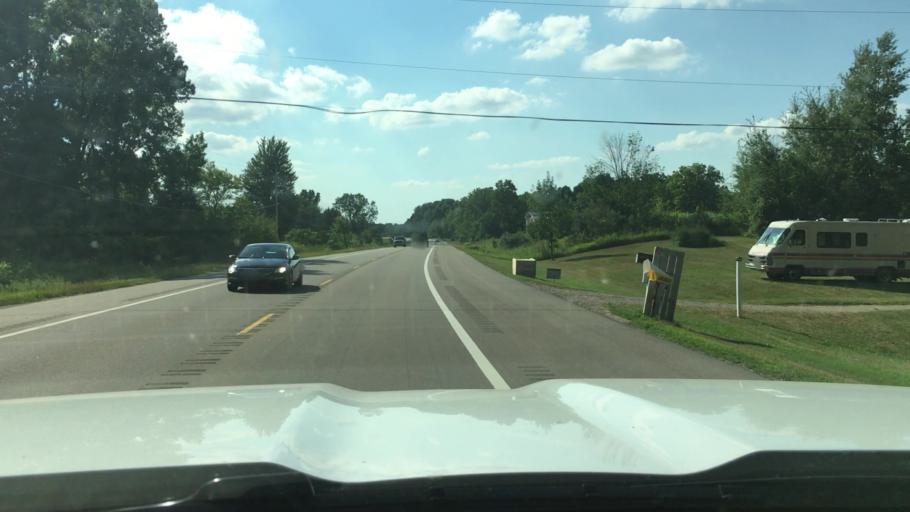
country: US
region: Michigan
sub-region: Kent County
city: Forest Hills
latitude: 43.0838
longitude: -85.4175
